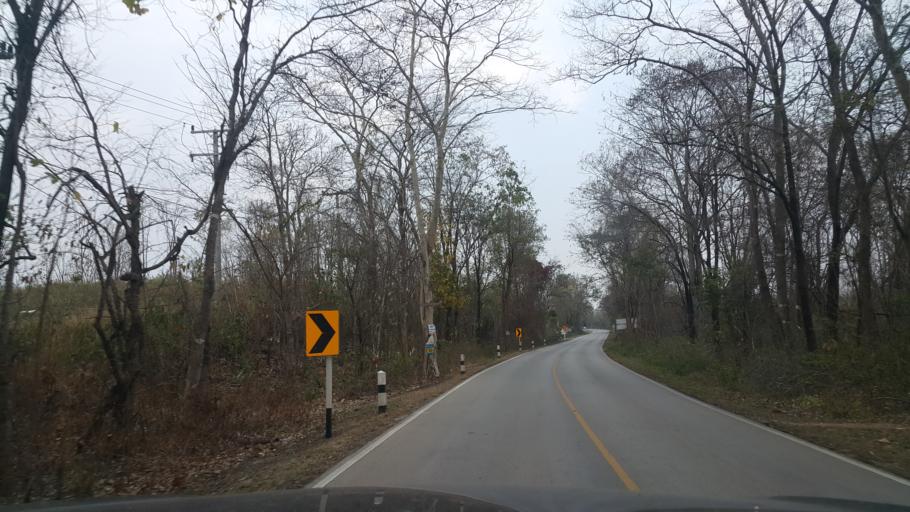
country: TH
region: Lampang
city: Soem Ngam
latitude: 17.9799
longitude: 99.1626
